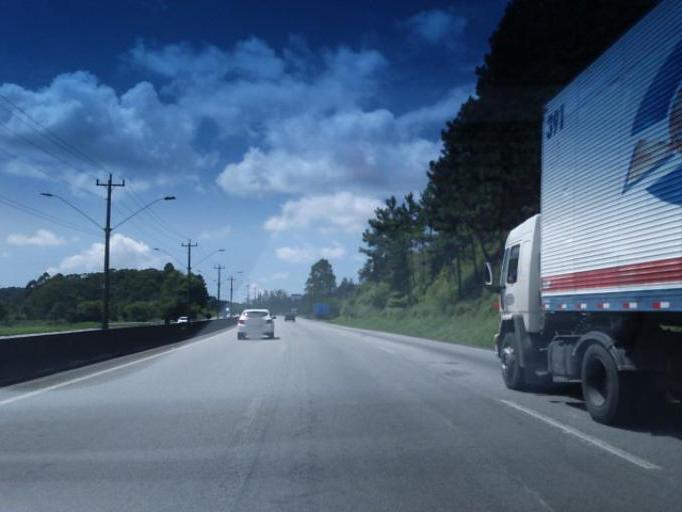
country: BR
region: Sao Paulo
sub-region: Sao Lourenco Da Serra
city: Sao Lourenco da Serra
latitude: -23.7812
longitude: -46.9156
